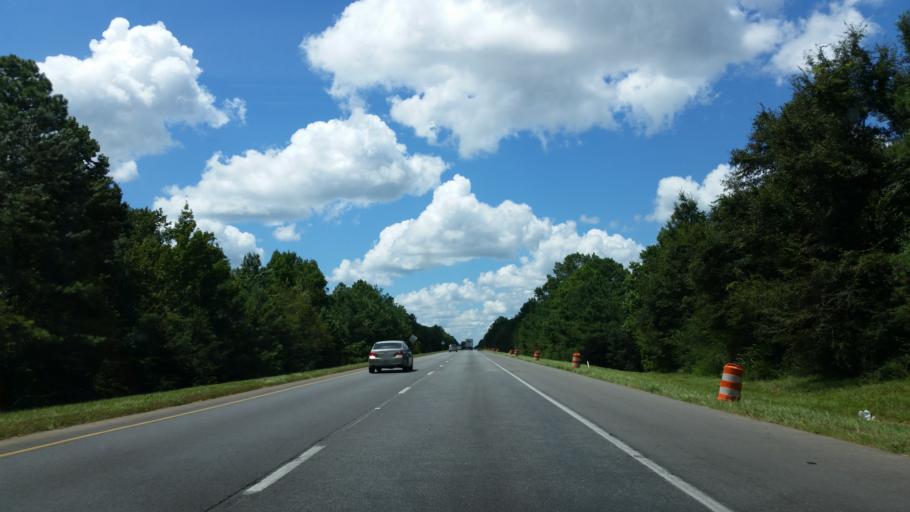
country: US
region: Alabama
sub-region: Baldwin County
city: Loxley
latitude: 30.6558
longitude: -87.8014
